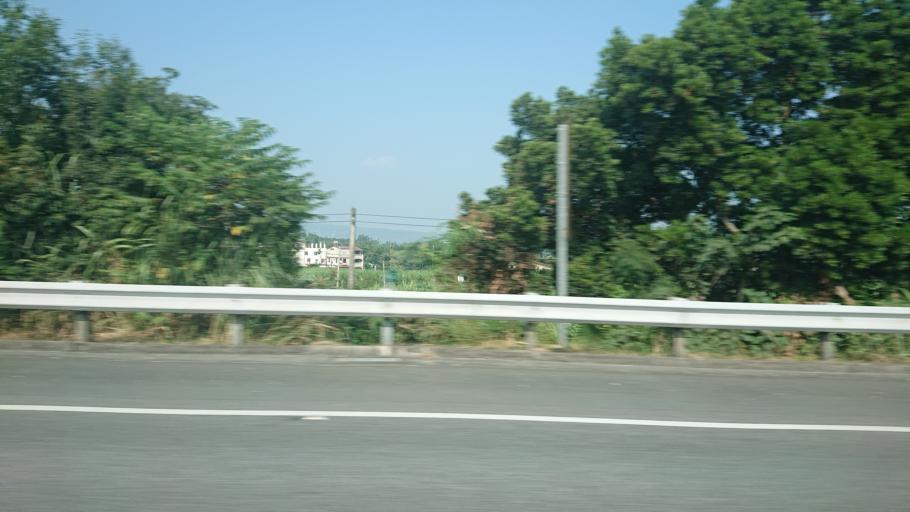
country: TW
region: Taiwan
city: Lugu
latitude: 23.7797
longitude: 120.7005
